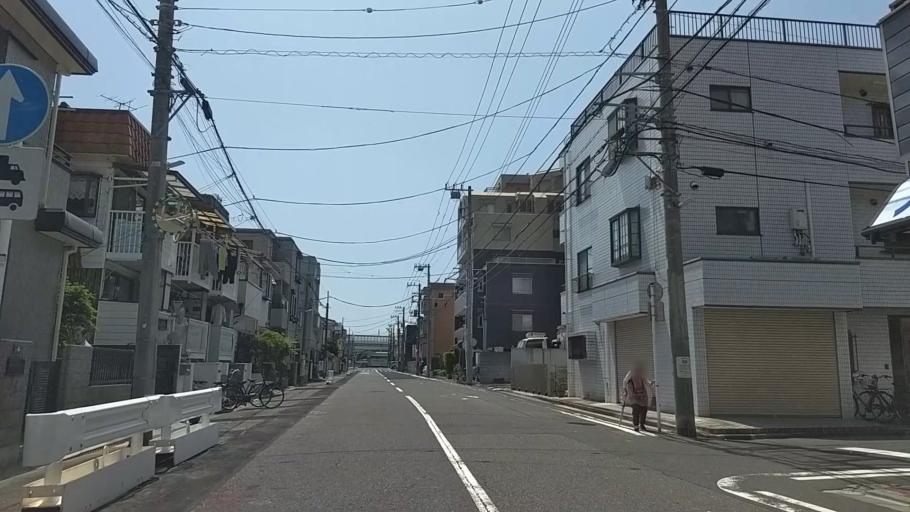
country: JP
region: Kanagawa
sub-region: Kawasaki-shi
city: Kawasaki
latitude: 35.5050
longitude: 139.6986
